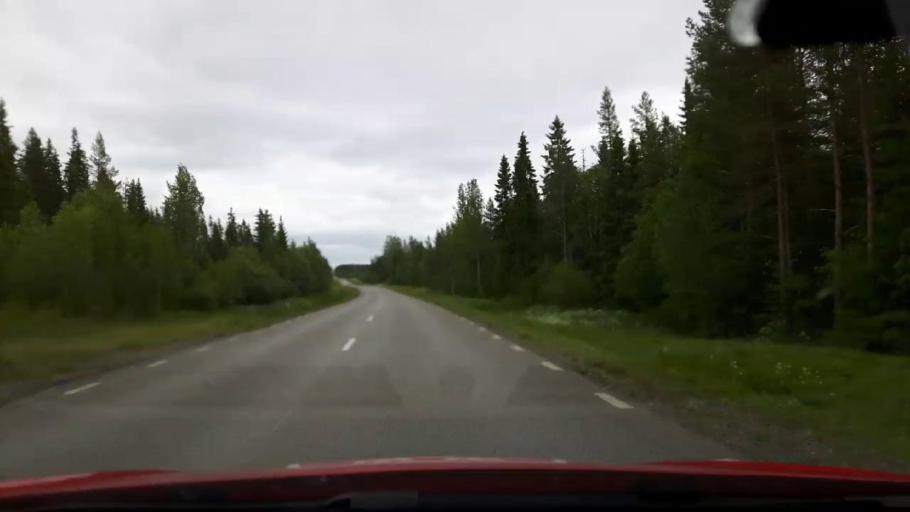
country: SE
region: Jaemtland
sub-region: OEstersunds Kommun
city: Lit
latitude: 63.7305
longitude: 14.9108
